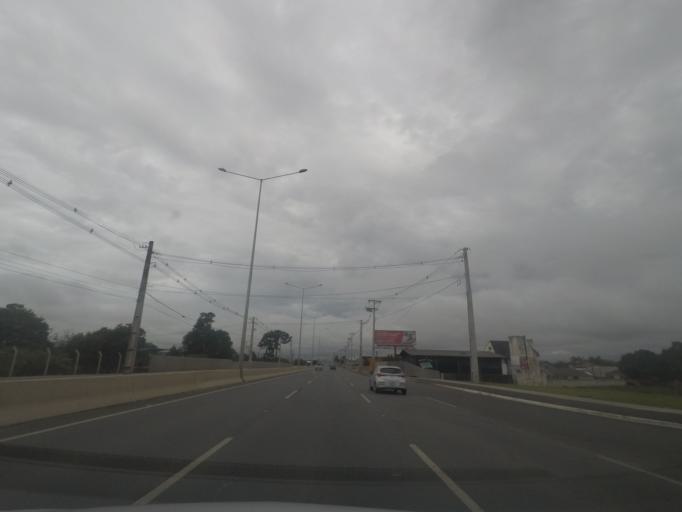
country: BR
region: Parana
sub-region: Pinhais
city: Pinhais
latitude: -25.4416
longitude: -49.1513
